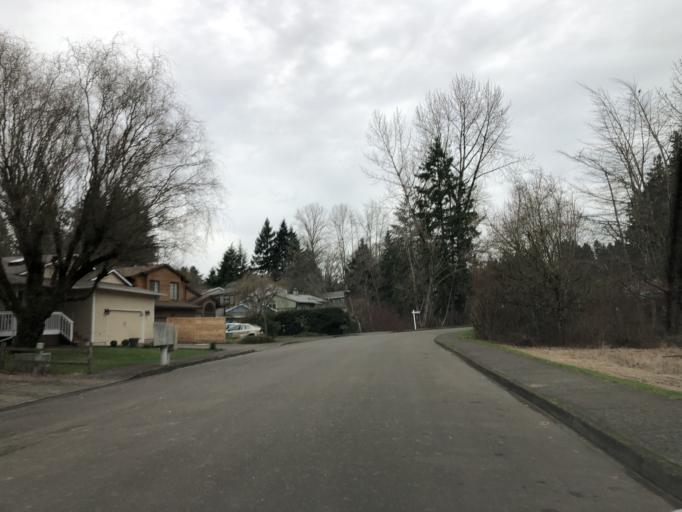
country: US
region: Oregon
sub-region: Washington County
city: Tigard
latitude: 45.4282
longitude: -122.7862
